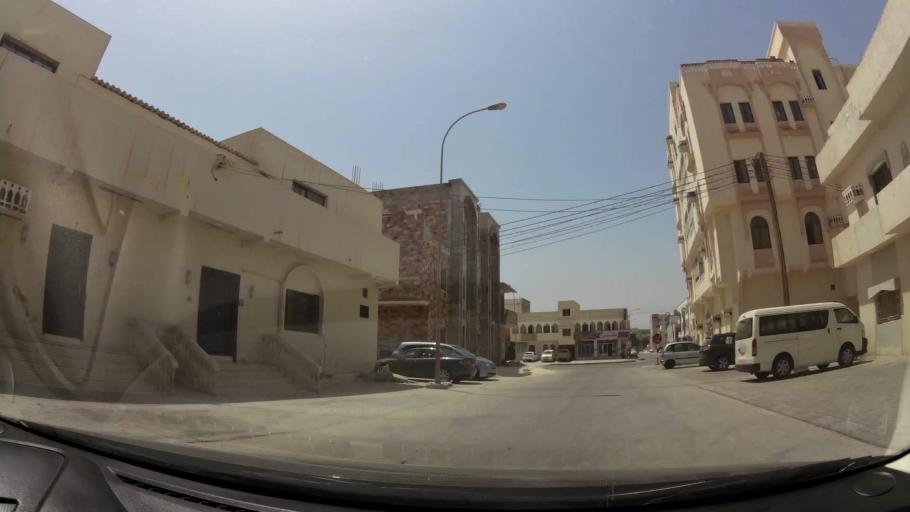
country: OM
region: Zufar
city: Salalah
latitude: 17.0170
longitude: 54.0839
